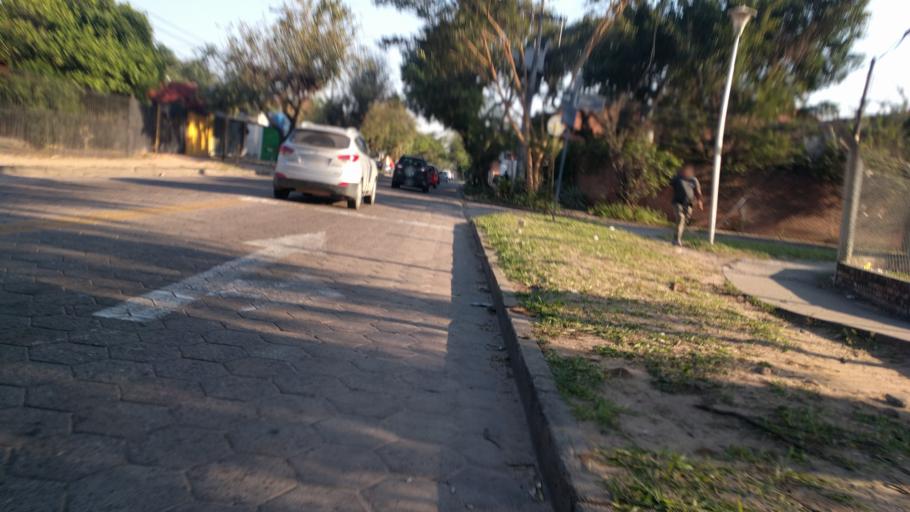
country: BO
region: Santa Cruz
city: Santa Cruz de la Sierra
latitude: -17.8070
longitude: -63.1724
